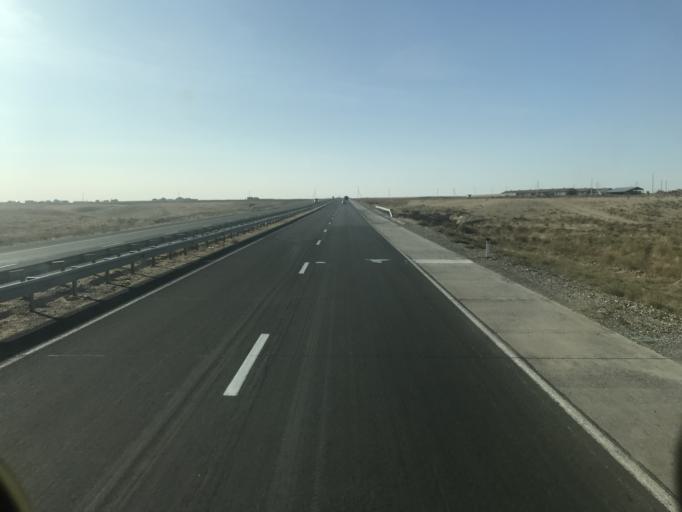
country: KZ
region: Ongtustik Qazaqstan
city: Temirlanovka
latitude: 42.5248
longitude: 69.3778
